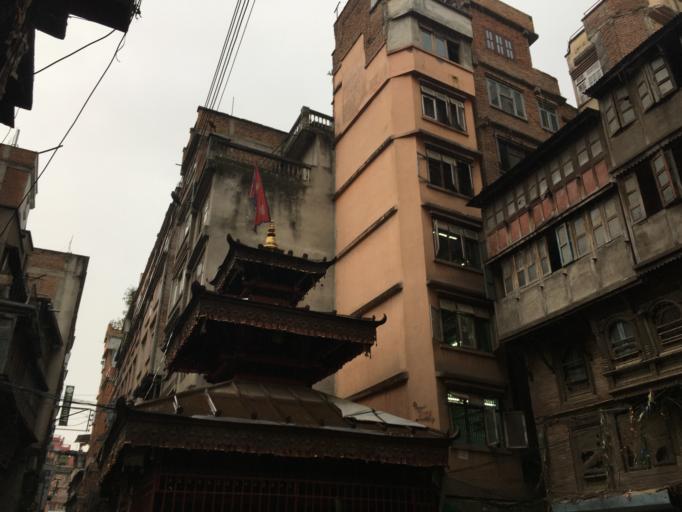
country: NP
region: Central Region
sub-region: Bagmati Zone
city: Kathmandu
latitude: 27.7078
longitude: 85.3112
